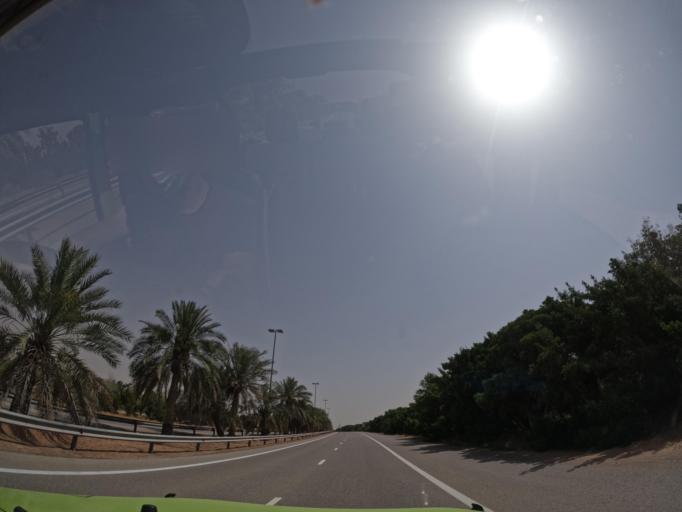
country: OM
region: Al Buraimi
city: Al Buraymi
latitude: 24.7014
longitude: 55.7522
